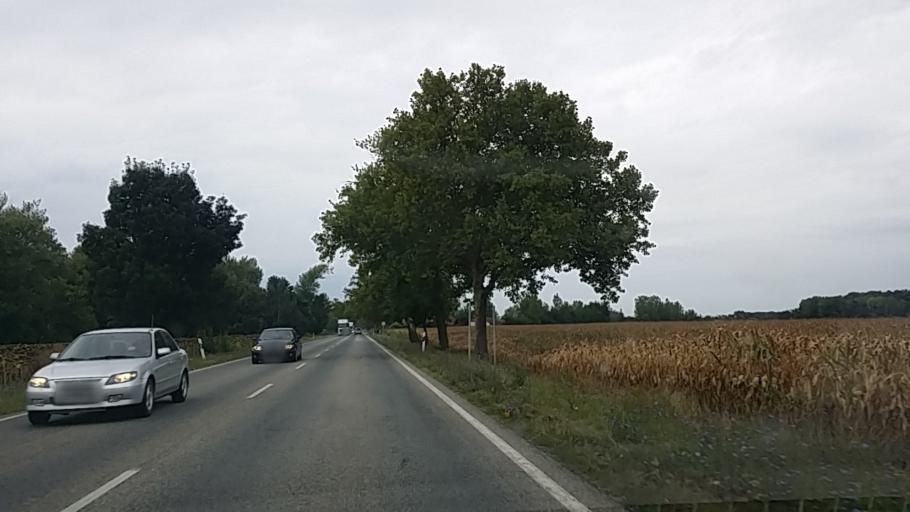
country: HU
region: Gyor-Moson-Sopron
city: Kapuvar
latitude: 47.5879
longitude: 17.0930
